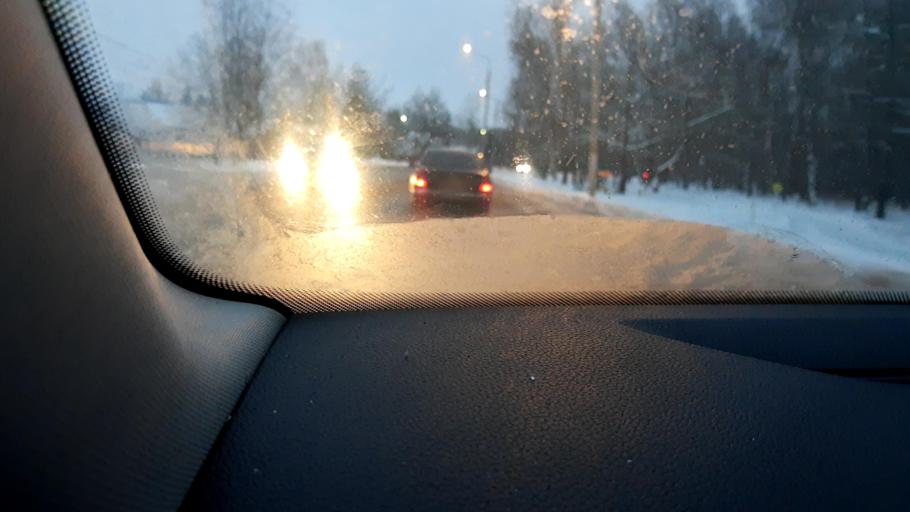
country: RU
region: Moskovskaya
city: Troitsk
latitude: 55.3084
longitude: 37.1823
